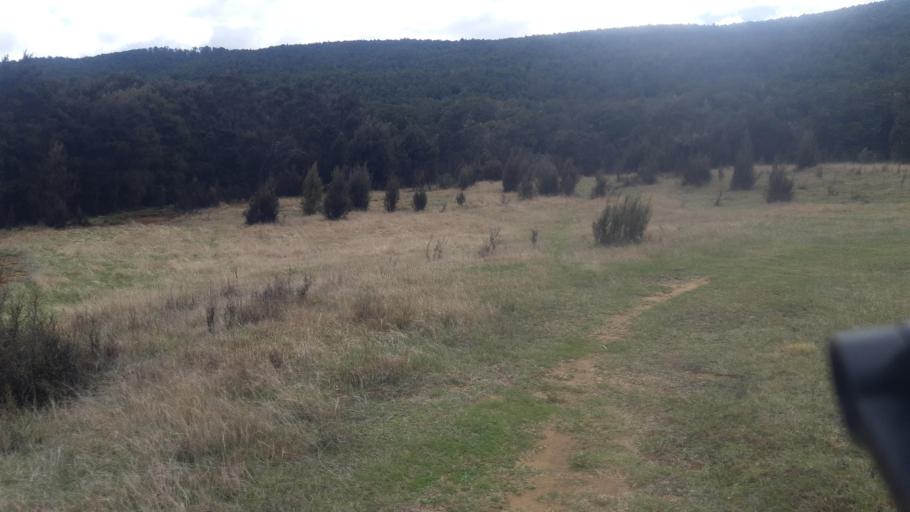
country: NZ
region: Tasman
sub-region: Tasman District
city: Wakefield
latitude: -41.7822
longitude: 172.8177
